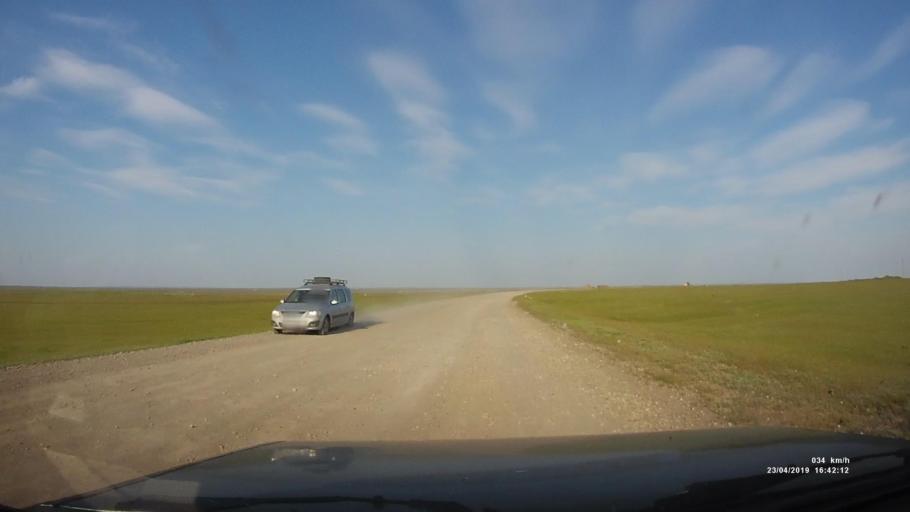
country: RU
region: Kalmykiya
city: Priyutnoye
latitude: 46.3475
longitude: 43.1919
